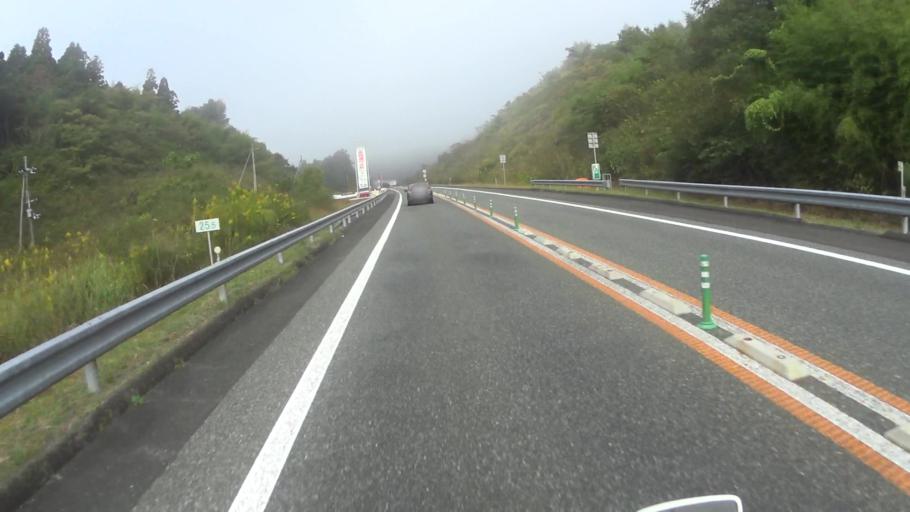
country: JP
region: Kyoto
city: Ayabe
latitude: 35.3417
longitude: 135.3032
